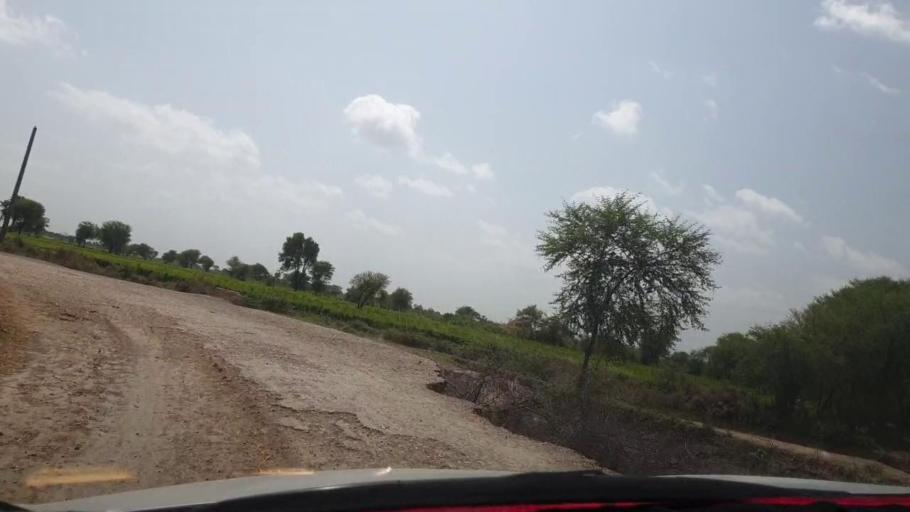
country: PK
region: Sindh
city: Talhar
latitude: 24.8958
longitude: 68.9060
